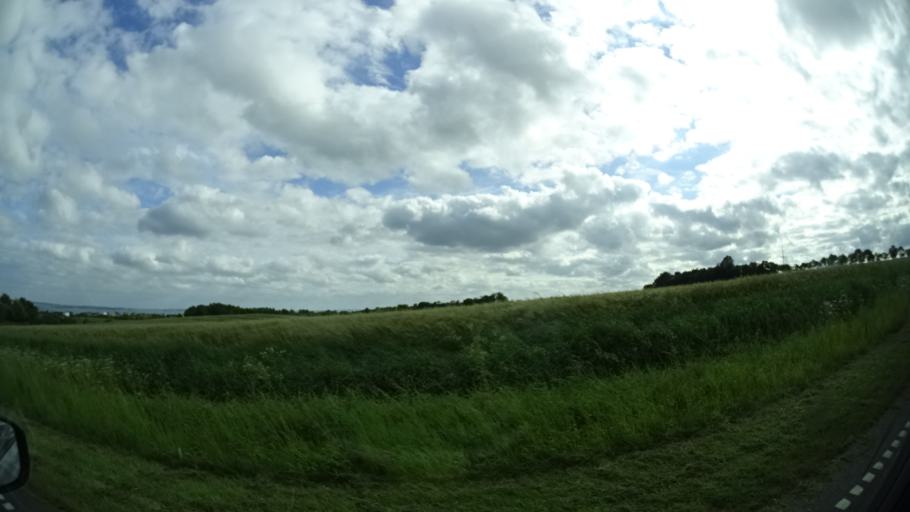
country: DK
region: Central Jutland
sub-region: Syddjurs Kommune
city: Ronde
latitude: 56.3175
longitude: 10.4216
